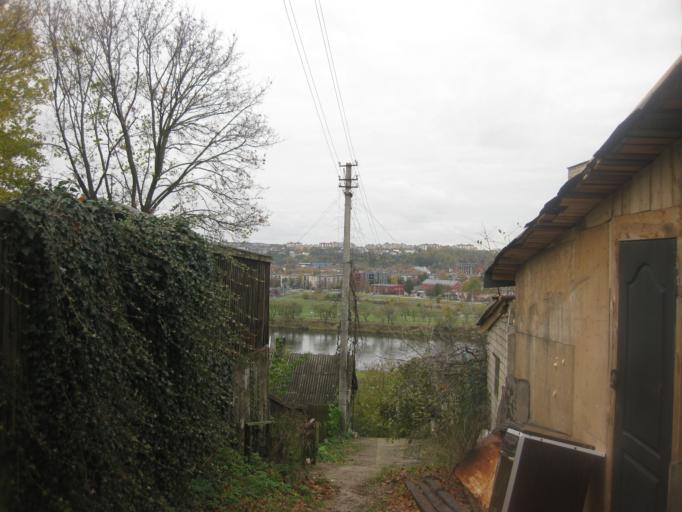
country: LT
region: Kauno apskritis
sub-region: Kaunas
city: Kaunas
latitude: 54.9078
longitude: 23.9083
